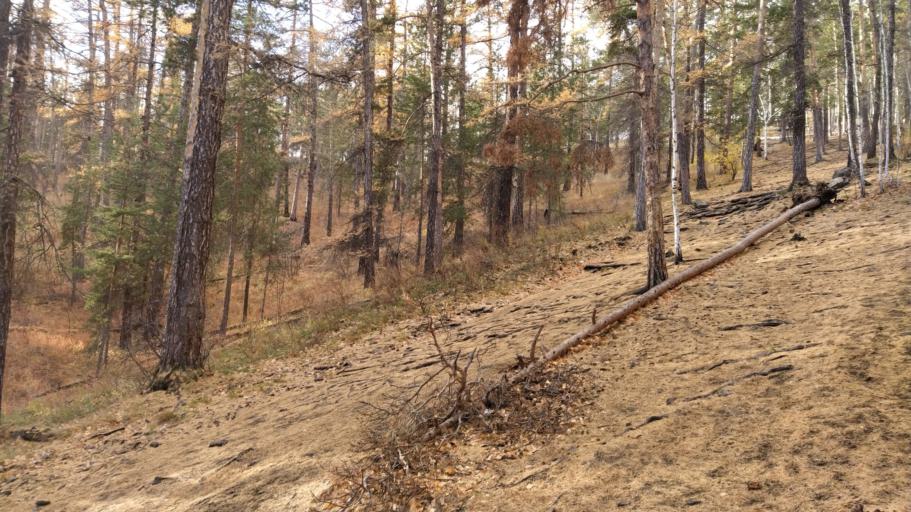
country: RU
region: Chelyabinsk
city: Kyshtym
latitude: 55.7210
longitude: 60.4517
